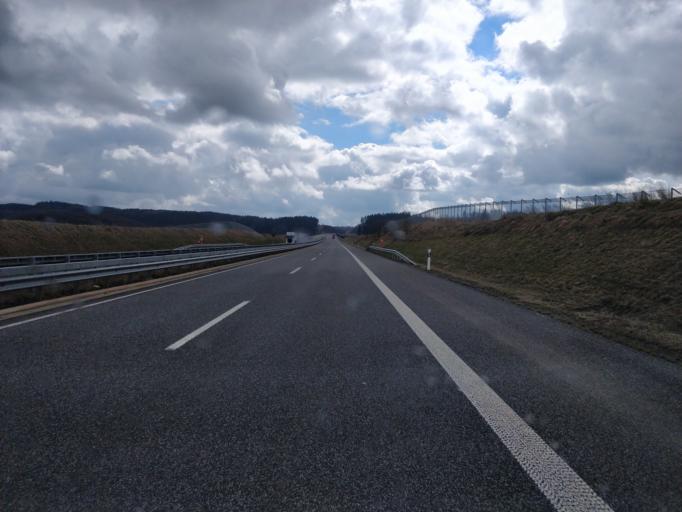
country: DE
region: Rheinland-Pfalz
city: Kradenbach
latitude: 50.2330
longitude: 6.8439
